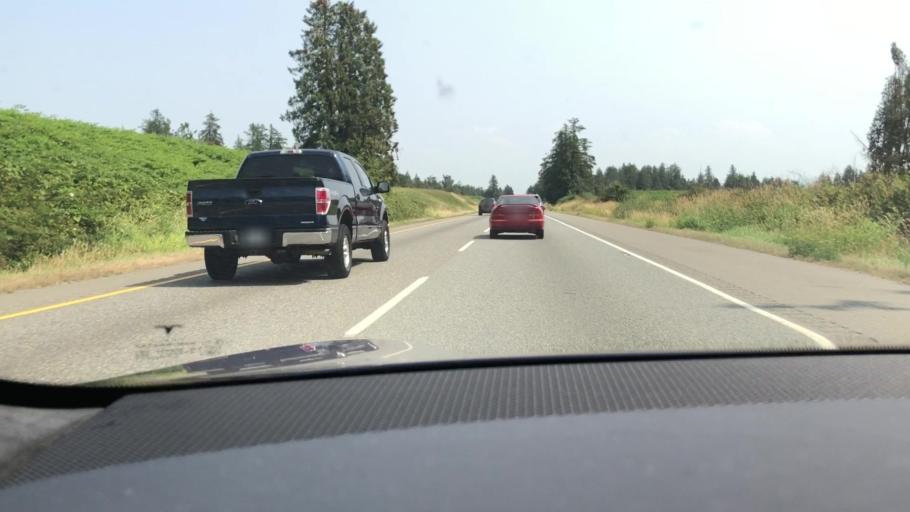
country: CA
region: British Columbia
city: Aldergrove
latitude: 49.0797
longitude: -122.4379
